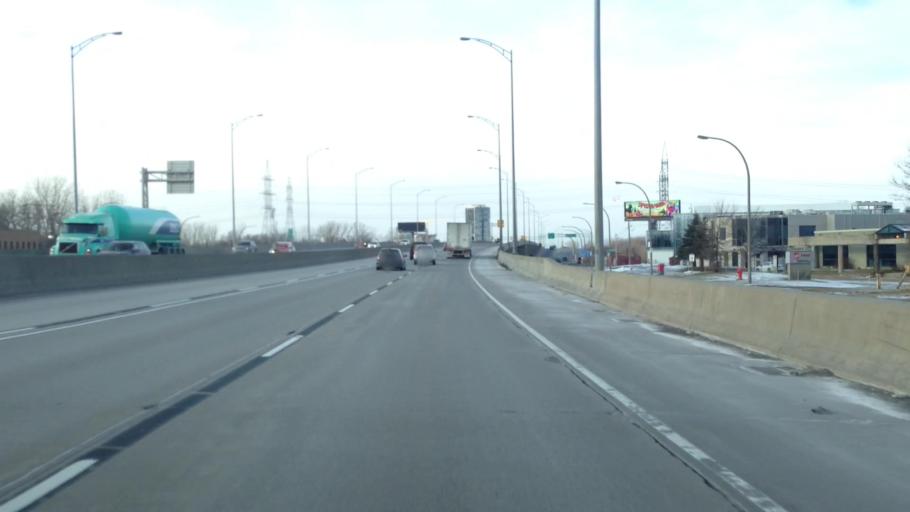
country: CA
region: Quebec
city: Dorval
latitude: 45.5017
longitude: -73.7544
